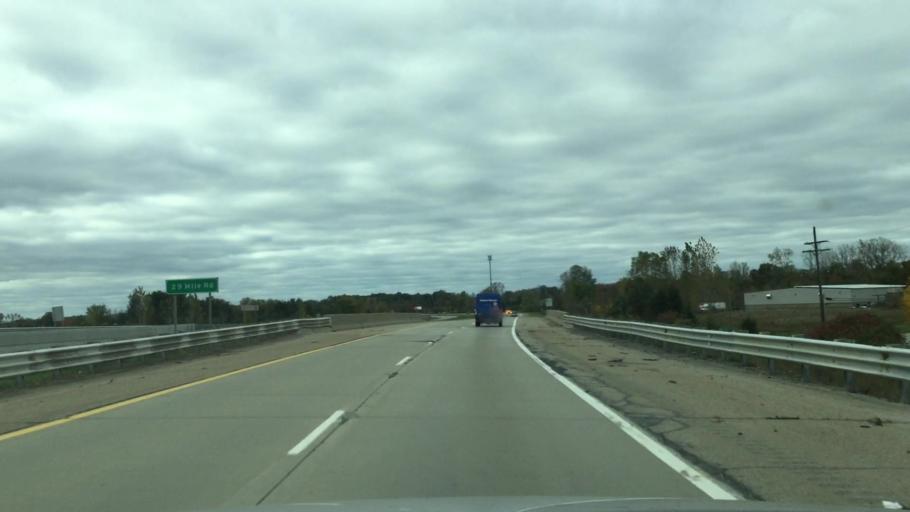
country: US
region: Michigan
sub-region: Macomb County
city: Romeo
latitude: 42.7581
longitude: -83.0126
